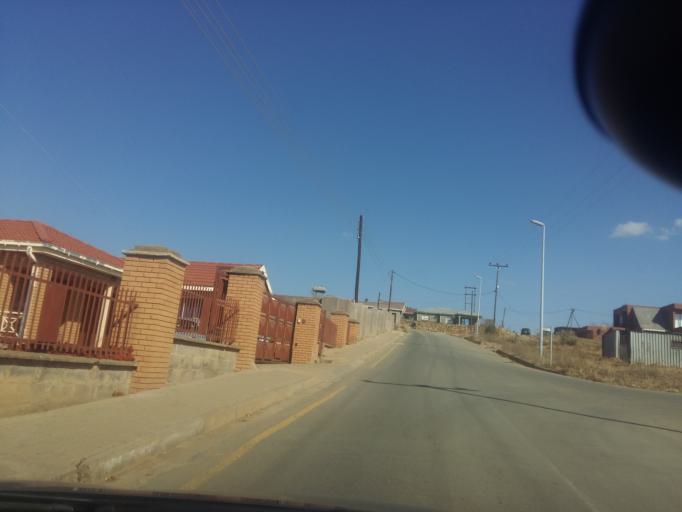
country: LS
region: Maseru
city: Maseru
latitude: -29.3476
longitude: 27.4505
